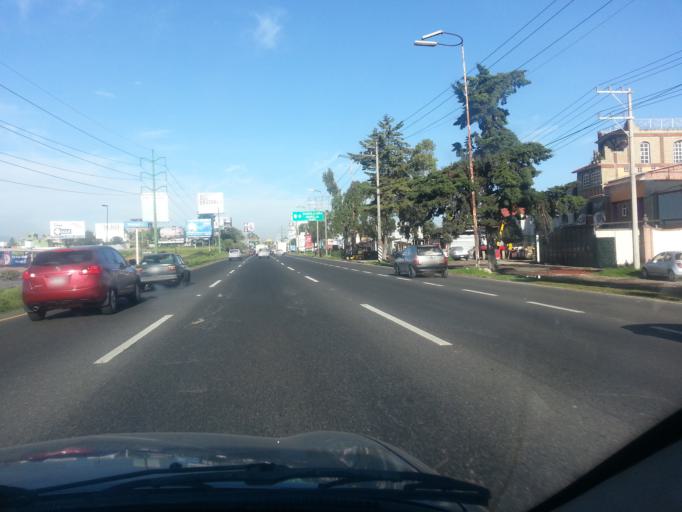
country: MX
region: Mexico
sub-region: Lerma
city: Nueva Ameyalco
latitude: 19.2841
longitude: -99.5016
